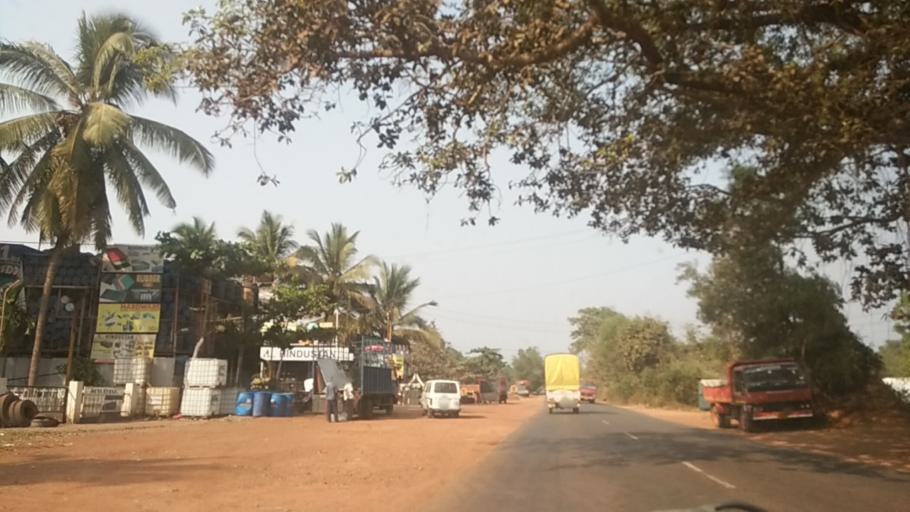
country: IN
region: Goa
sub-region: North Goa
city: Colovale
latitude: 15.6199
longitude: 73.8228
